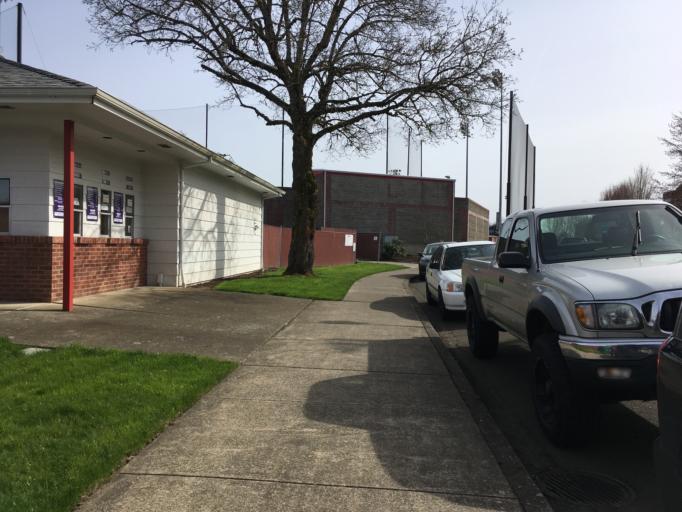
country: US
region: Oregon
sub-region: Yamhill County
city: McMinnville
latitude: 45.1985
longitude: -123.1980
